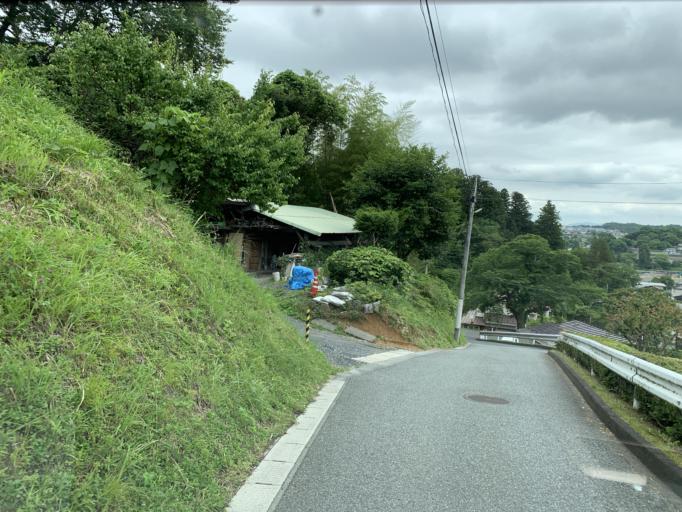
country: JP
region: Iwate
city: Ichinoseki
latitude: 38.9226
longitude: 141.1294
